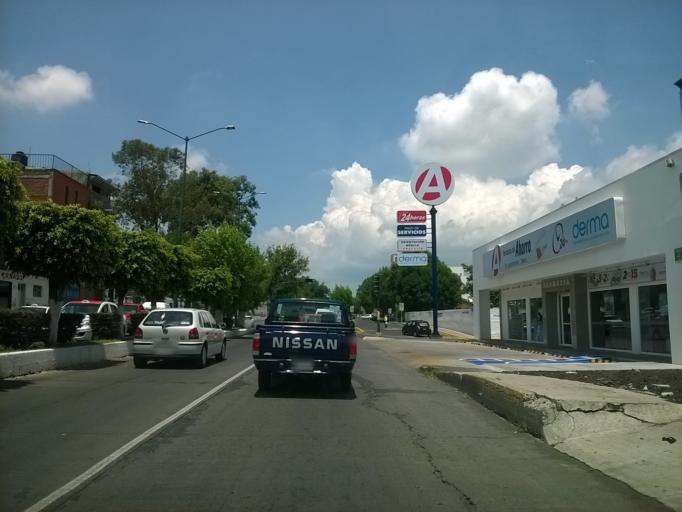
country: MX
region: Michoacan
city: Morelia
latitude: 19.7073
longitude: -101.1935
